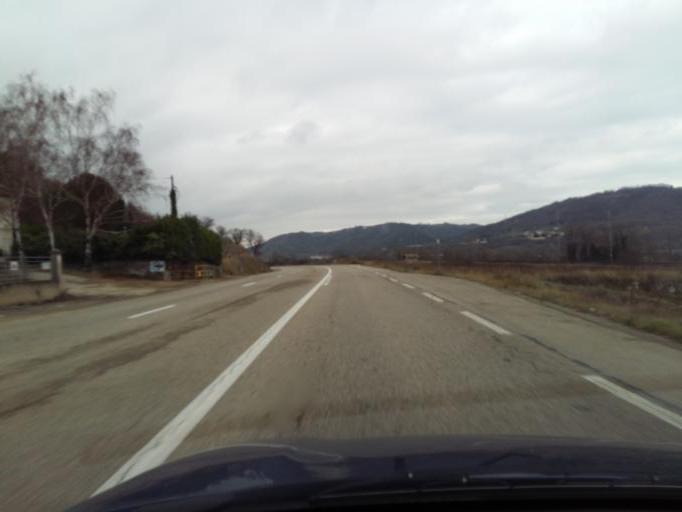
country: FR
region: Rhone-Alpes
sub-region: Departement de la Drome
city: Saint-Vallier
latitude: 45.1469
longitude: 4.8151
